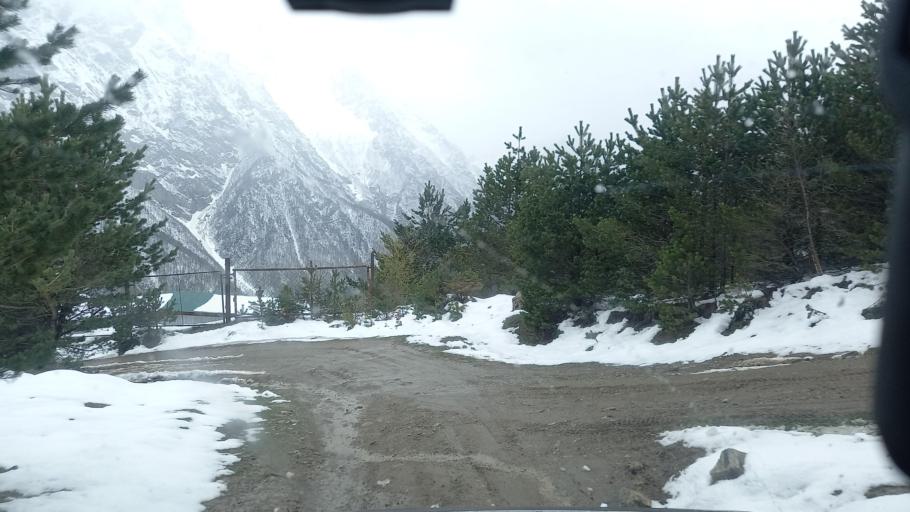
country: RU
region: North Ossetia
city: Mizur
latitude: 42.8106
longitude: 43.9562
